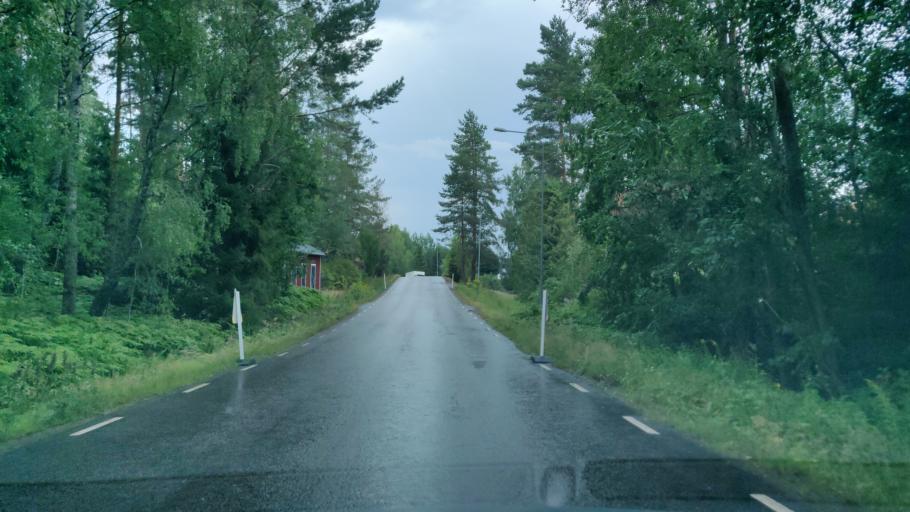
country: SE
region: Vaermland
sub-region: Munkfors Kommun
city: Munkfors
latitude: 59.8431
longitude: 13.5311
